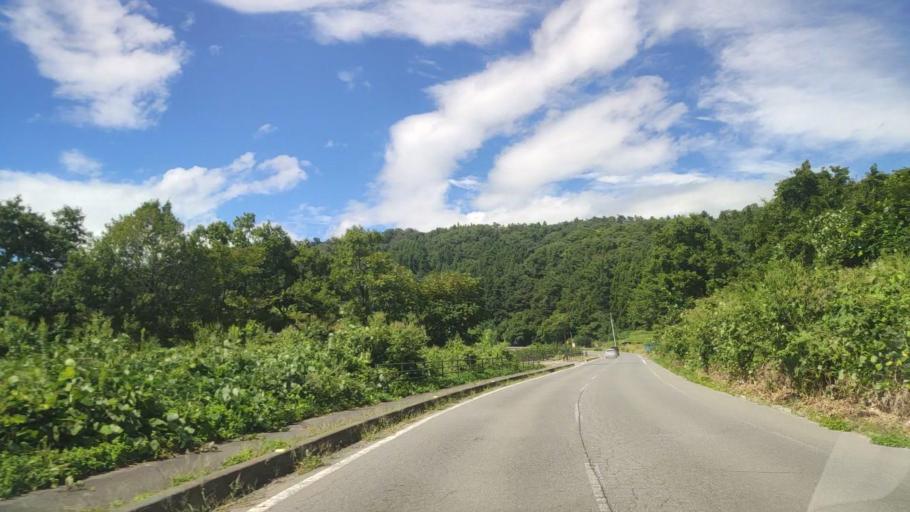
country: JP
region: Nagano
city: Suzaka
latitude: 36.7194
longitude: 138.2791
